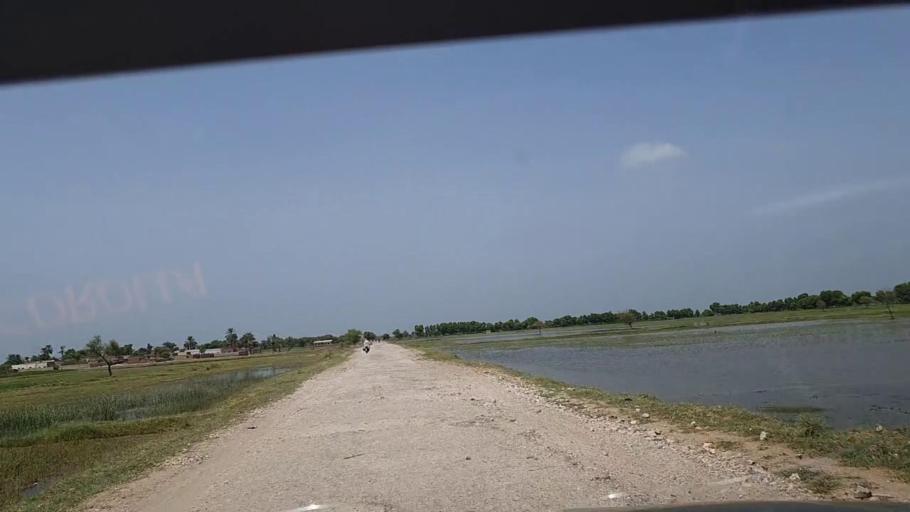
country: PK
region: Sindh
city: Khanpur
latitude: 27.8212
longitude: 69.4442
